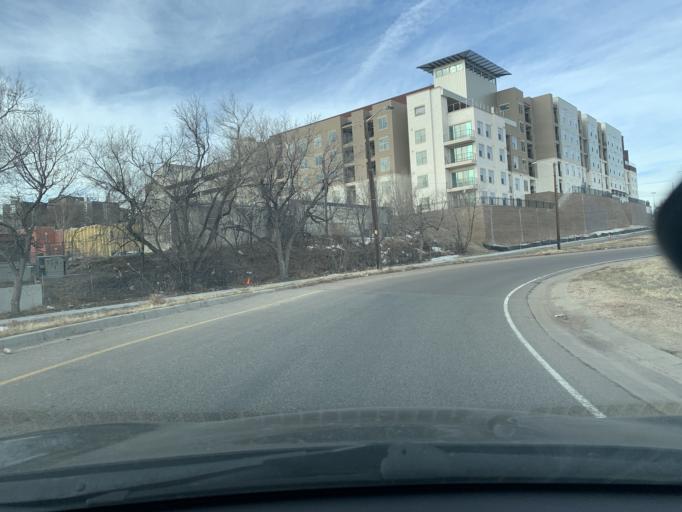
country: US
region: Colorado
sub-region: Jefferson County
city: Edgewater
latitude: 39.7394
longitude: -105.0259
